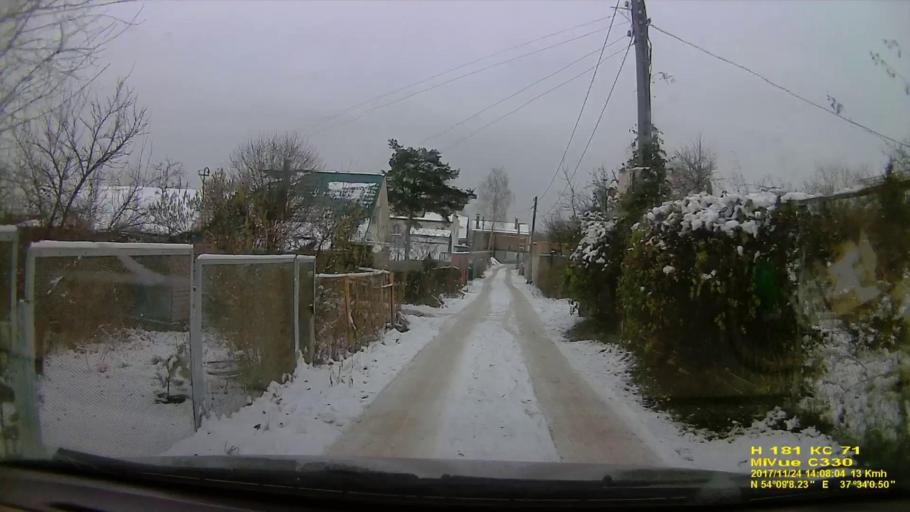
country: RU
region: Tula
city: Mendeleyevskiy
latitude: 54.1528
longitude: 37.5616
